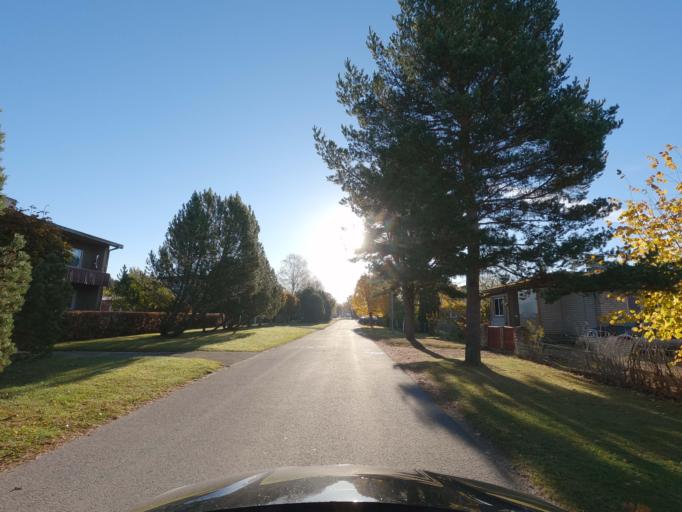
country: EE
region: Raplamaa
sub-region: Kohila vald
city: Kohila
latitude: 59.1672
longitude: 24.7616
